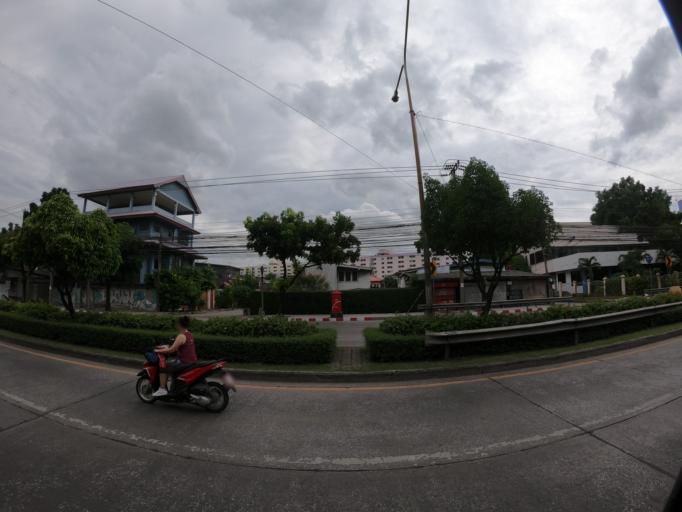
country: TH
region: Bangkok
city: Bang Kapi
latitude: 13.7746
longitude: 100.6456
